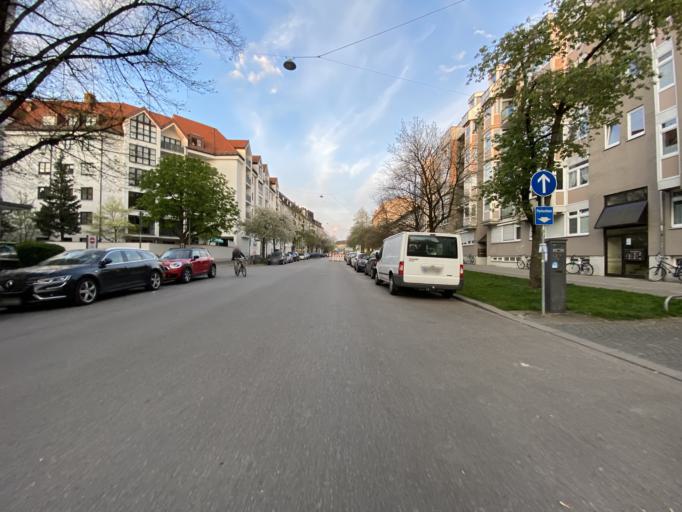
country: DE
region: Bavaria
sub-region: Upper Bavaria
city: Munich
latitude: 48.1596
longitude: 11.5443
